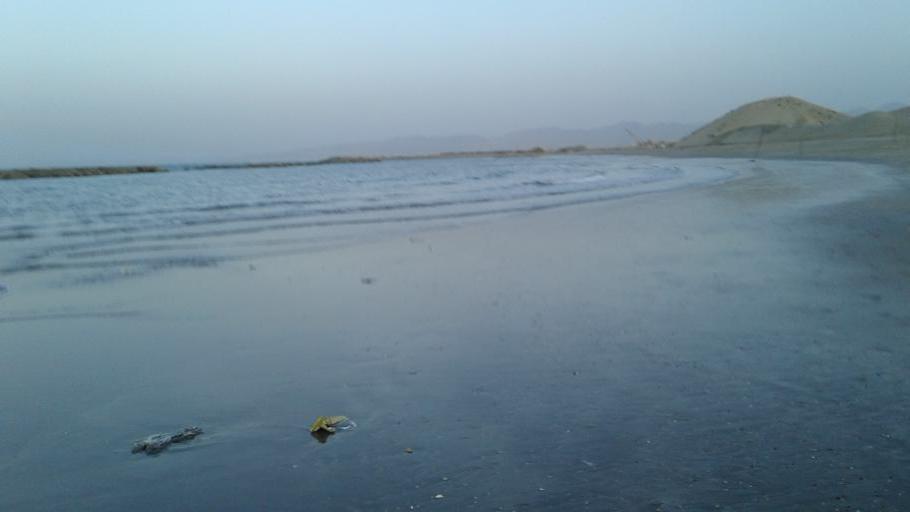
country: OM
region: Muhafazat Masqat
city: As Sib al Jadidah
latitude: 23.6241
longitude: 58.2773
